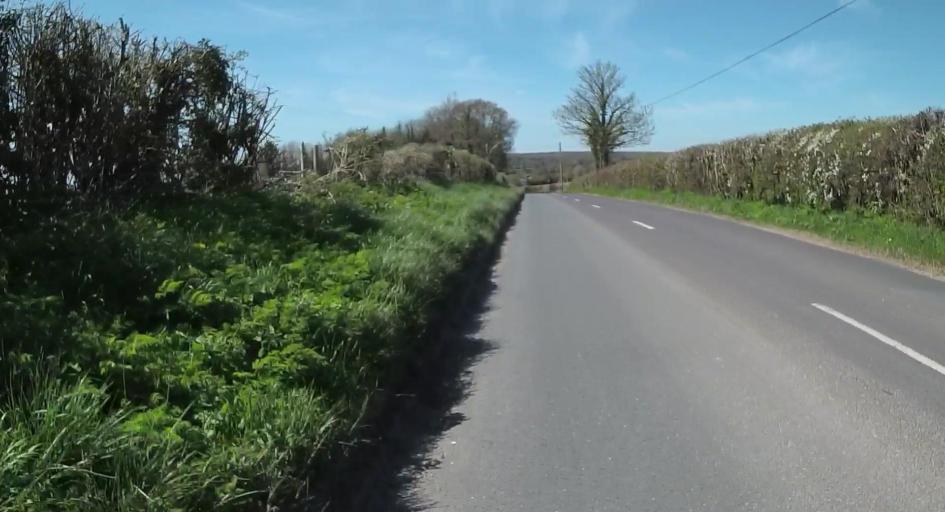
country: GB
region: England
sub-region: Hampshire
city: Winchester
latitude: 51.1036
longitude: -1.3728
